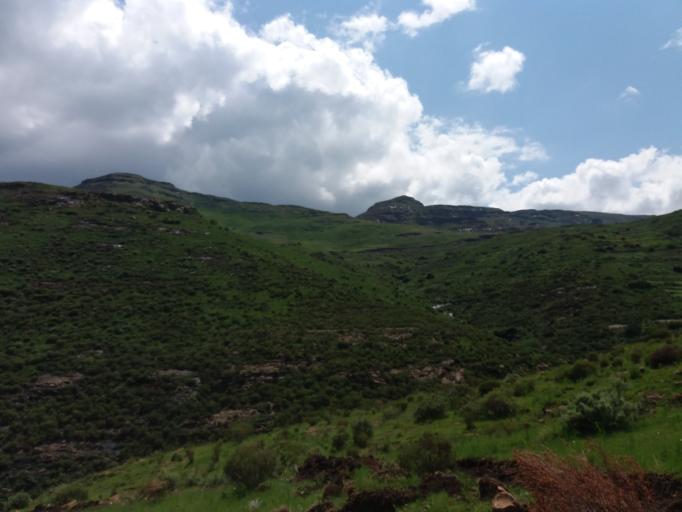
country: LS
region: Maseru
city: Nako
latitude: -29.6731
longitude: 27.9129
